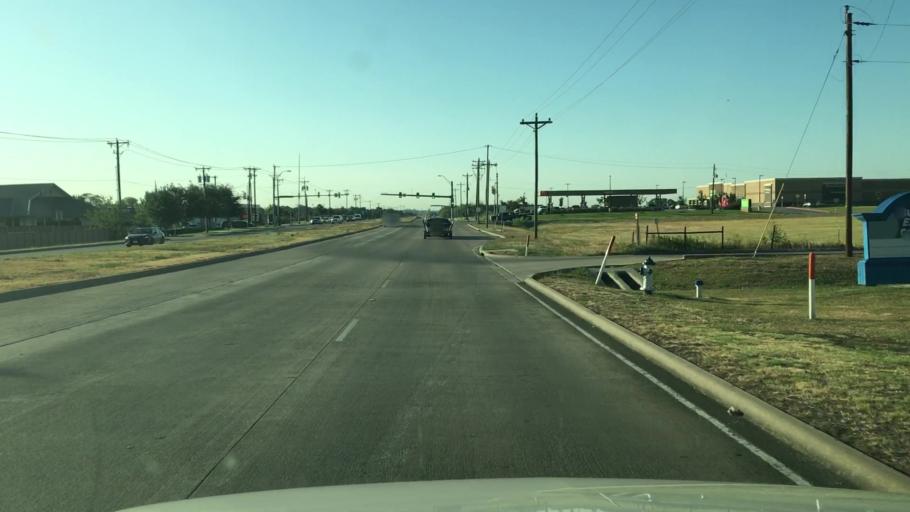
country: US
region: Texas
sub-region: Tarrant County
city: Crowley
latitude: 32.5404
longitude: -97.3626
